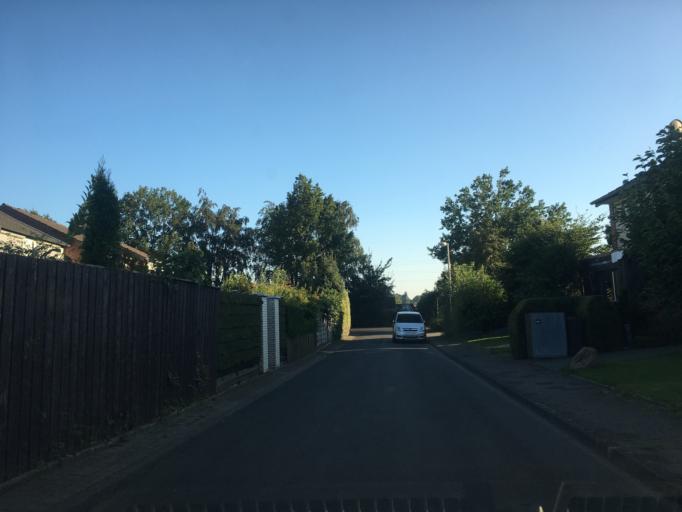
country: DE
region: North Rhine-Westphalia
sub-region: Regierungsbezirk Munster
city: Muenster
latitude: 51.9250
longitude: 7.6019
